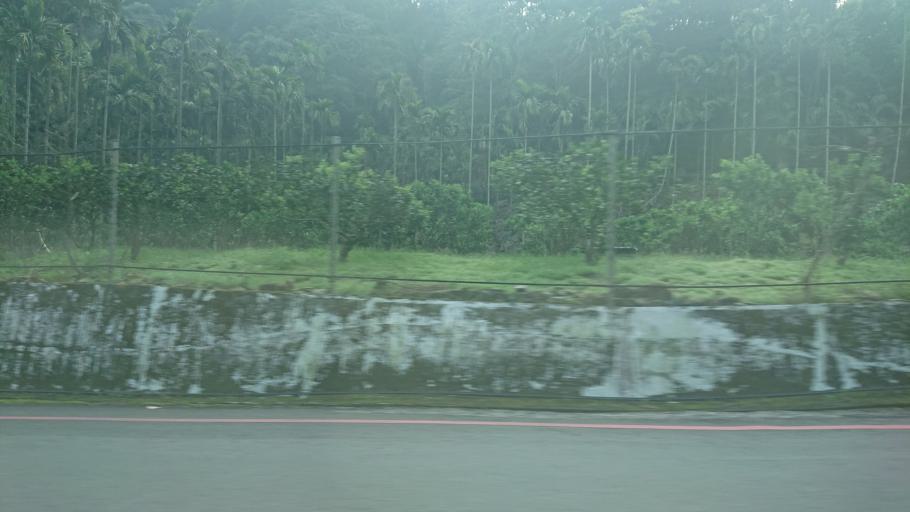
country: TW
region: Taiwan
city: Daxi
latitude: 24.8630
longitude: 121.4217
